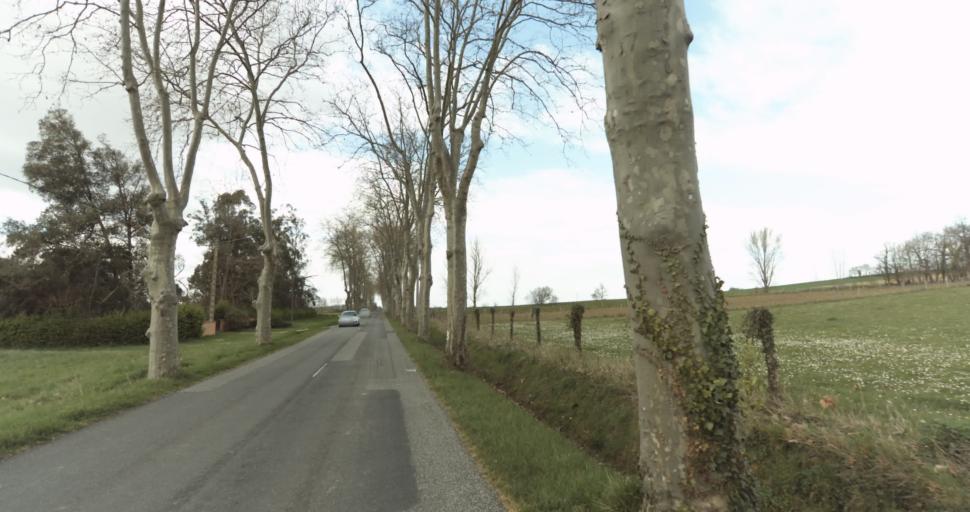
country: FR
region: Midi-Pyrenees
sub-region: Departement de la Haute-Garonne
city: Auterive
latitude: 43.3715
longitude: 1.4690
